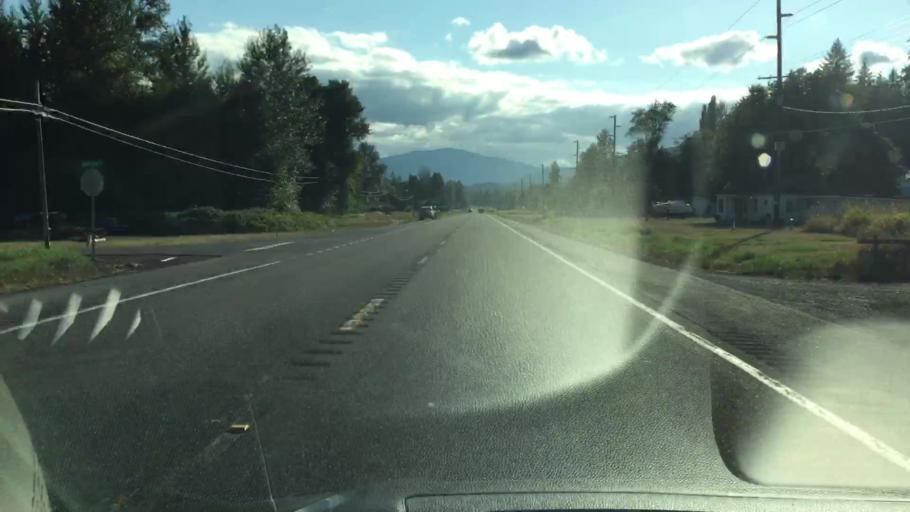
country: US
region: Washington
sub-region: Lewis County
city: Morton
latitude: 46.5328
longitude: -122.1249
